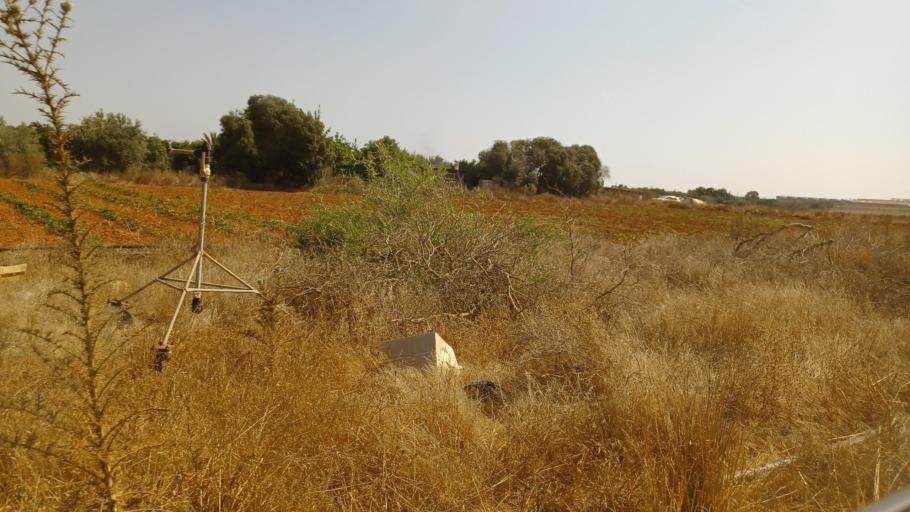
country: CY
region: Ammochostos
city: Deryneia
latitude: 35.0685
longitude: 33.9486
